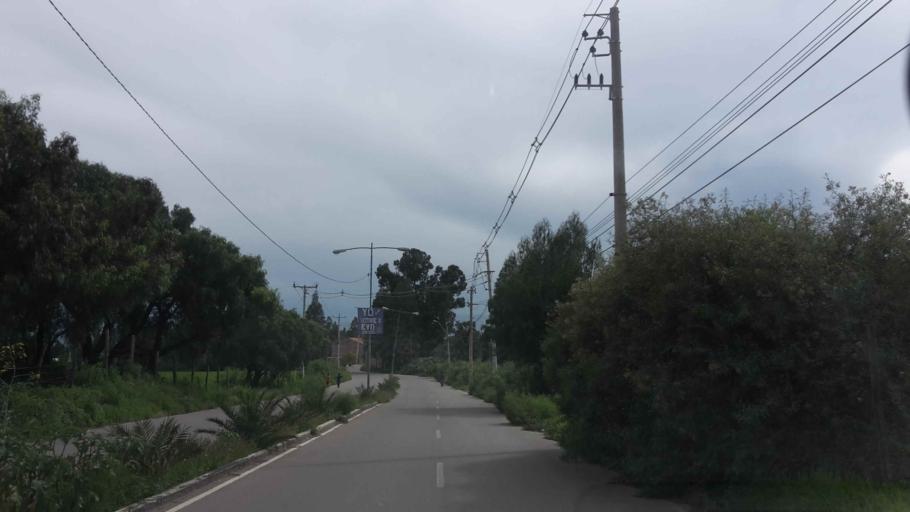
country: BO
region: Cochabamba
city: Cochabamba
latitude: -17.3305
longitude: -66.2489
